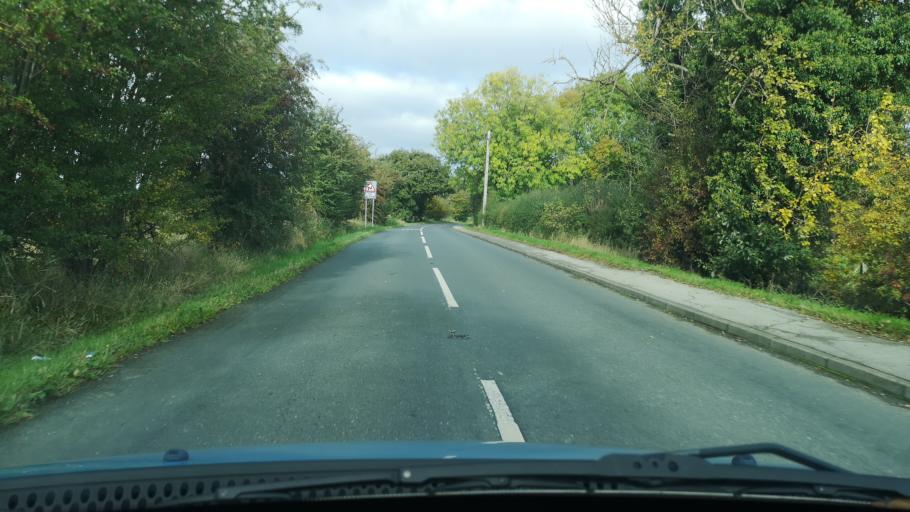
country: GB
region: England
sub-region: City and Borough of Wakefield
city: Featherstone
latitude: 53.6851
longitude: -1.3842
